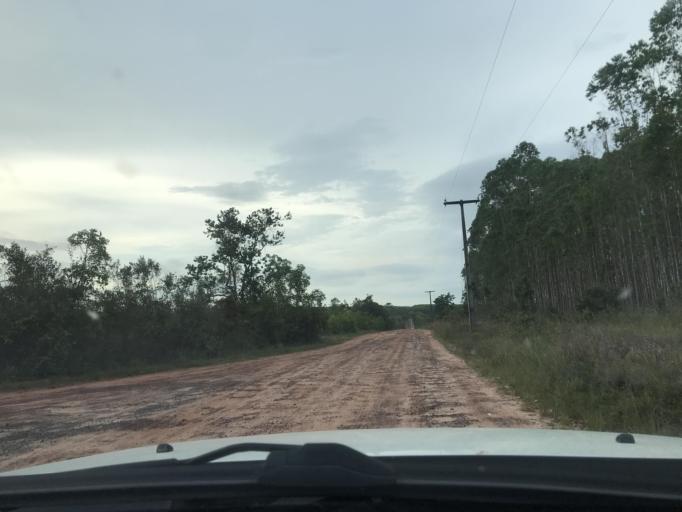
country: BR
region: Bahia
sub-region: Entre Rios
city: Entre Rios
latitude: -12.0896
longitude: -38.2013
